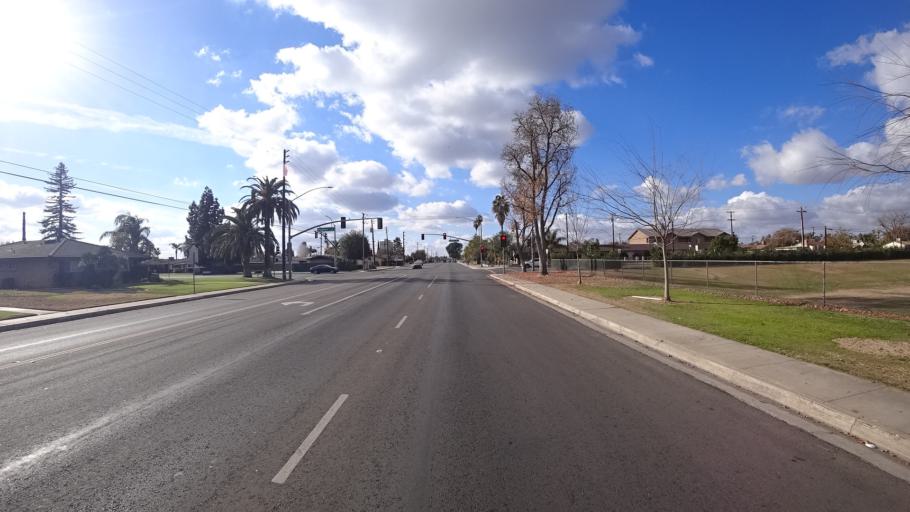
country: US
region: California
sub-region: Kern County
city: Bakersfield
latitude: 35.3322
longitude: -119.0295
